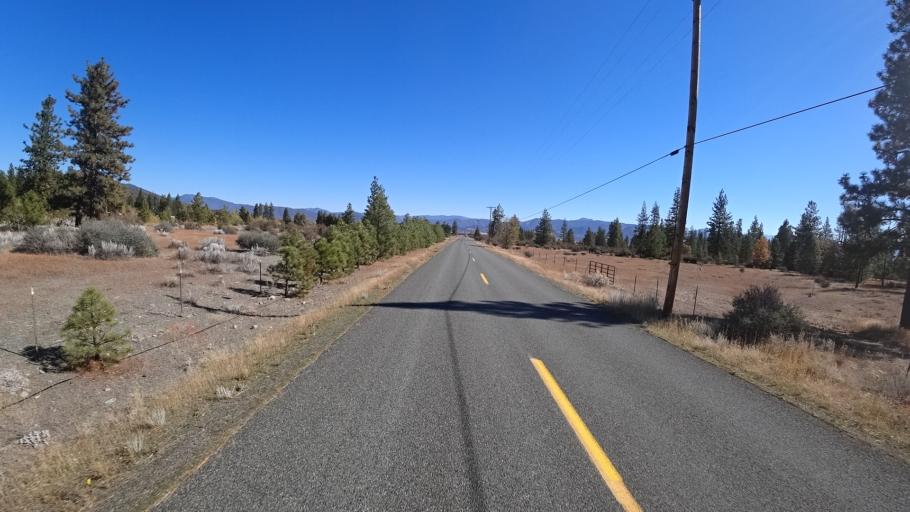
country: US
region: California
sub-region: Siskiyou County
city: Yreka
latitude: 41.5388
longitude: -122.9174
